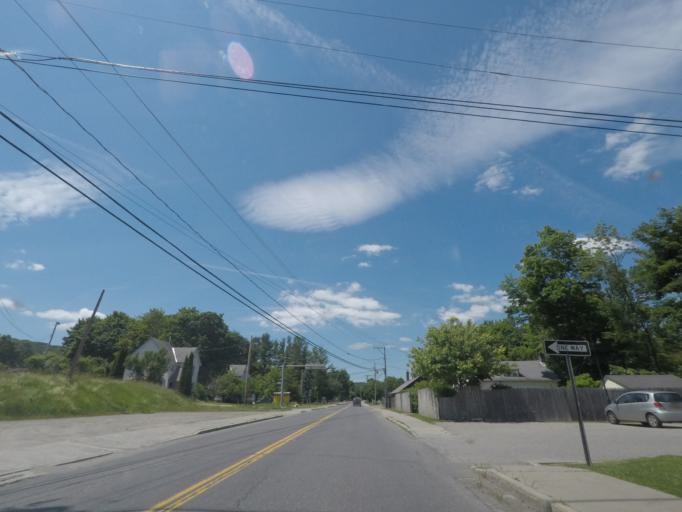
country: US
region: New York
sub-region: Dutchess County
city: Pine Plains
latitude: 41.9532
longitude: -73.5129
